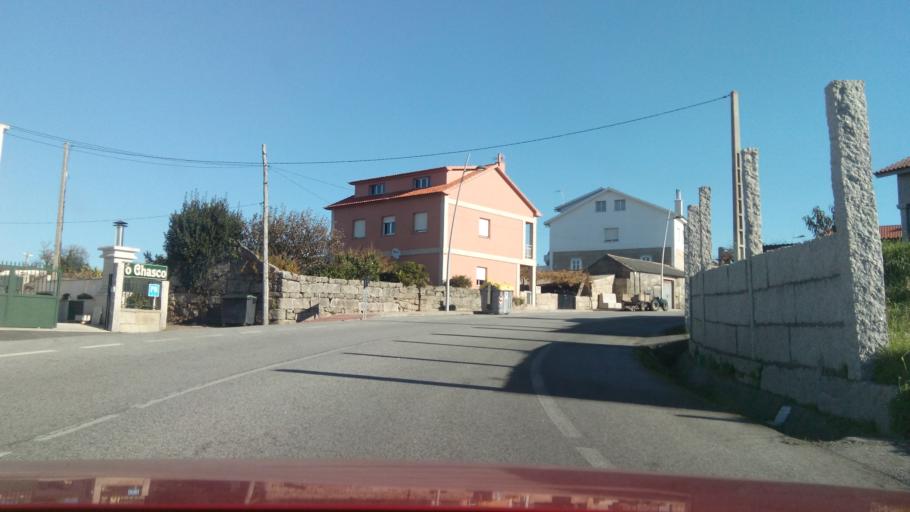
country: ES
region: Galicia
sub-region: Provincia de Pontevedra
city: O Grove
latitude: 42.4684
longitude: -8.9051
